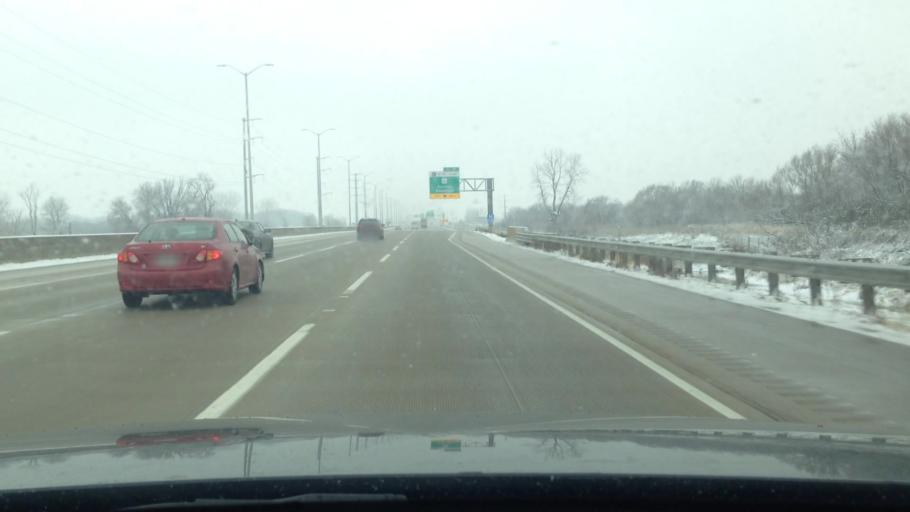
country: US
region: Illinois
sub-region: Kane County
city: Gilberts
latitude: 42.1137
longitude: -88.4149
